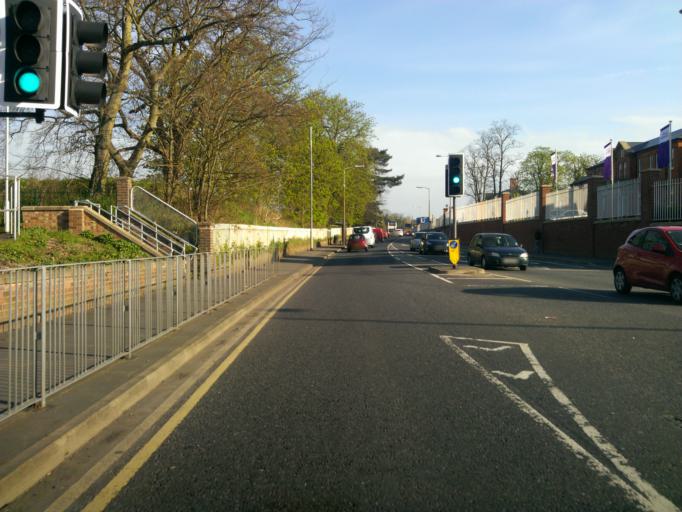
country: GB
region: England
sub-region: Essex
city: Colchester
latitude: 51.8807
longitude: 0.9038
